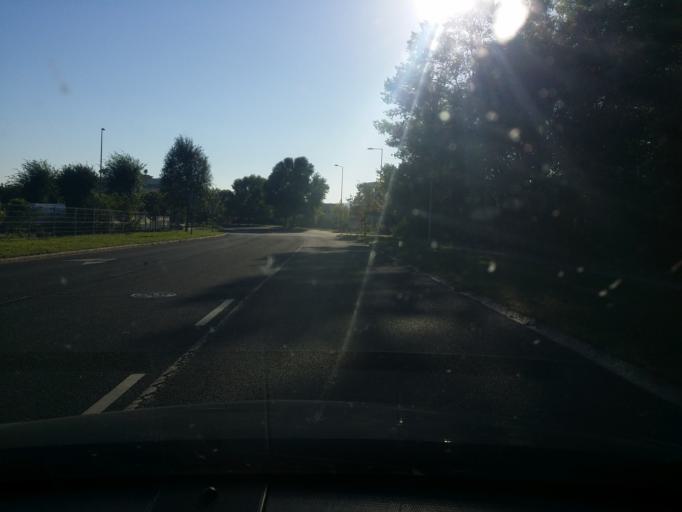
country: HU
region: Budapest
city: Budapest XV. keruelet
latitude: 47.5969
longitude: 19.1073
